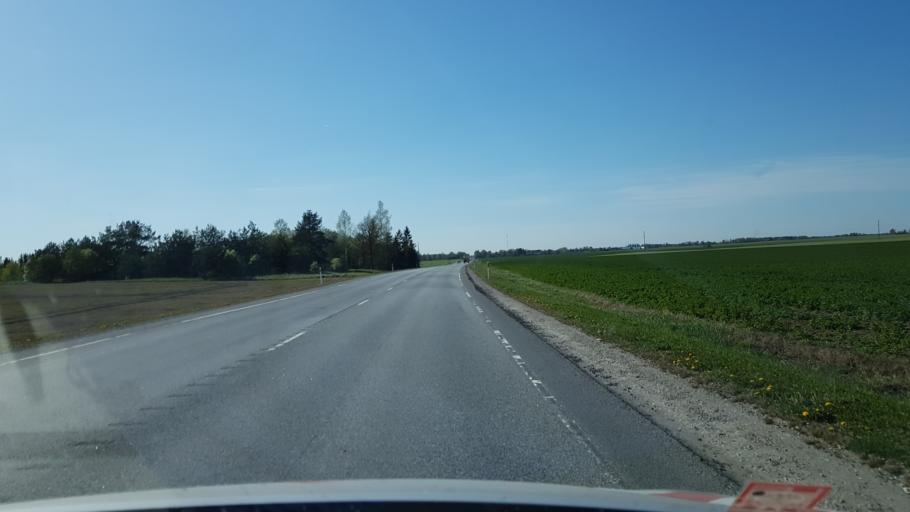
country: EE
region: Jogevamaa
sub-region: Poltsamaa linn
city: Poltsamaa
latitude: 58.6503
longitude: 26.0282
